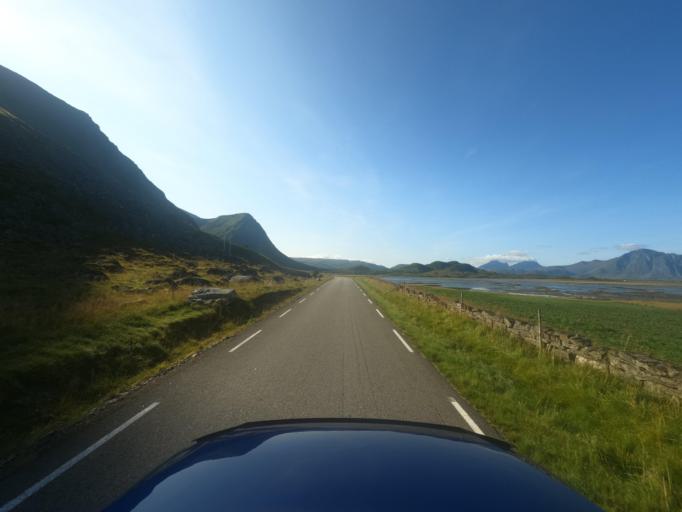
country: NO
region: Nordland
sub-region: Vestvagoy
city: Evjen
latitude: 68.3361
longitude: 13.9219
